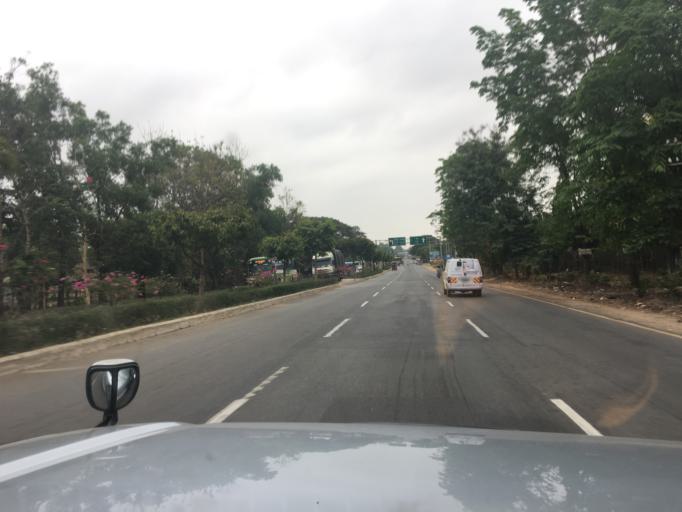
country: MM
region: Bago
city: Bago
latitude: 17.2438
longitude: 96.4648
